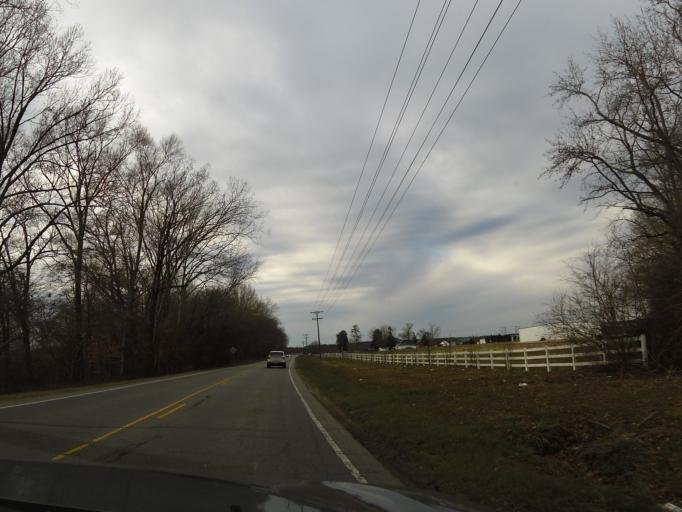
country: US
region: North Carolina
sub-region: Nash County
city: Rocky Mount
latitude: 35.9736
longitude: -77.7155
